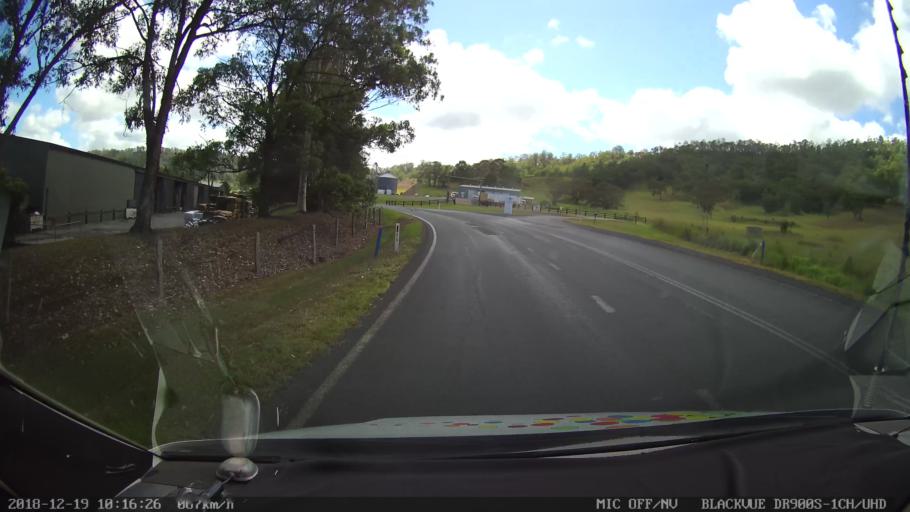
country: AU
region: New South Wales
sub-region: Kyogle
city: Kyogle
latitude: -28.6077
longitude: 153.0215
